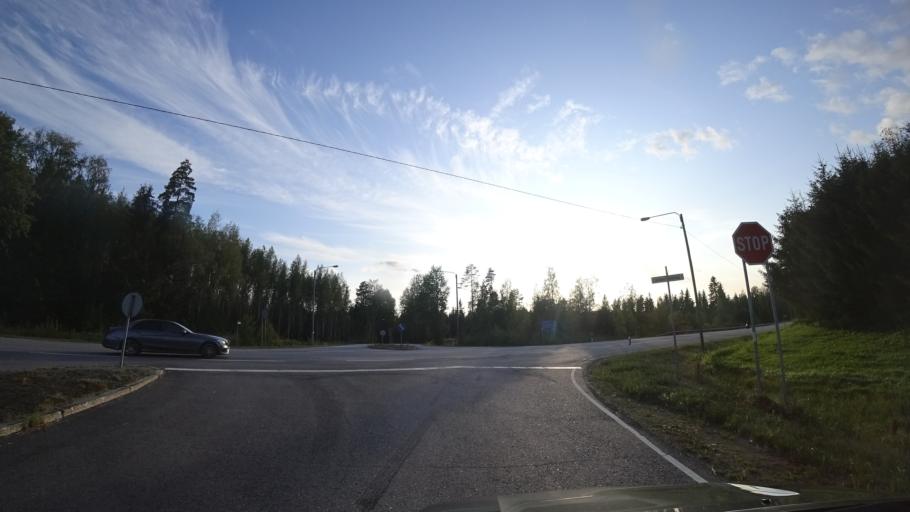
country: FI
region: Haeme
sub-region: Haemeenlinna
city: Lammi
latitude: 61.0632
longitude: 24.9799
